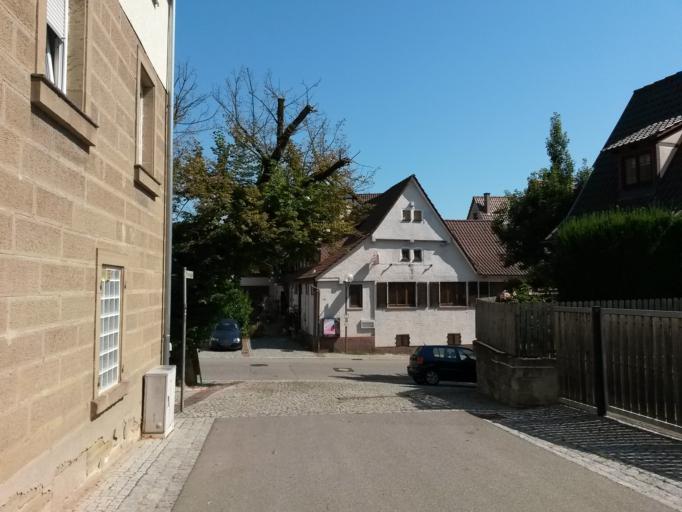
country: DE
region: Baden-Wuerttemberg
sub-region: Karlsruhe Region
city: Muhlacker
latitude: 48.9774
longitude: 8.8609
